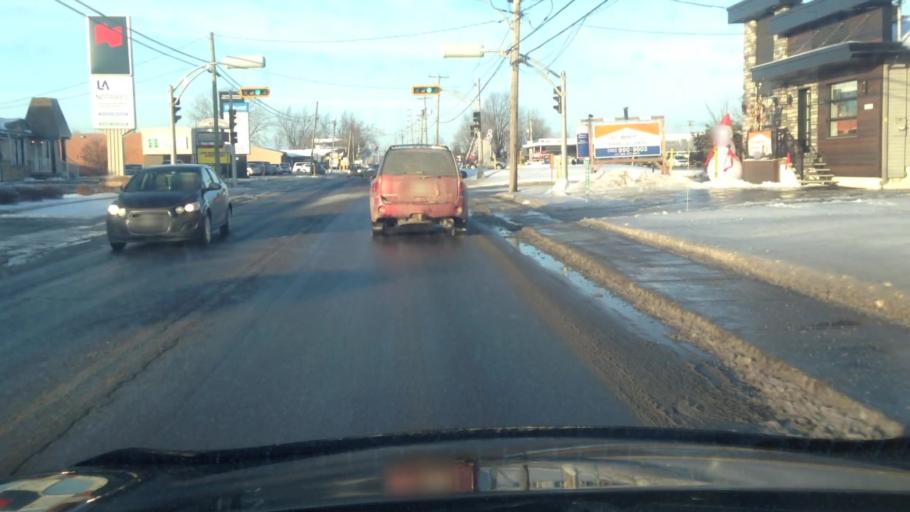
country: CA
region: Quebec
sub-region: Lanaudiere
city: Saint-Lin-Laurentides
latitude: 45.8651
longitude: -73.7571
